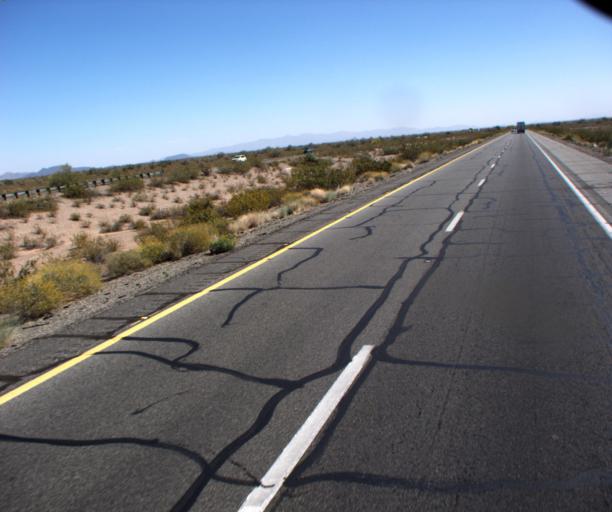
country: US
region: Arizona
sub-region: Maricopa County
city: Buckeye
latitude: 33.5132
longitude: -113.0278
